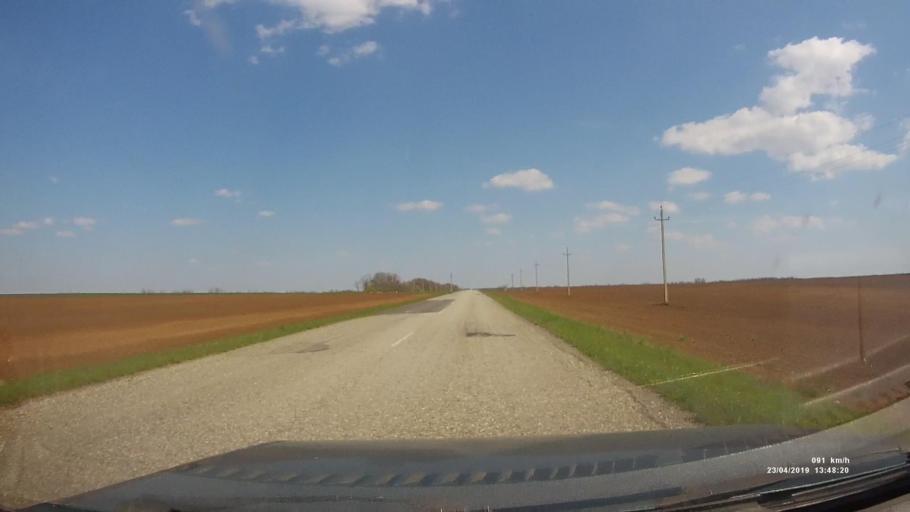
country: RU
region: Kalmykiya
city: Yashalta
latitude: 46.5991
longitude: 42.8716
